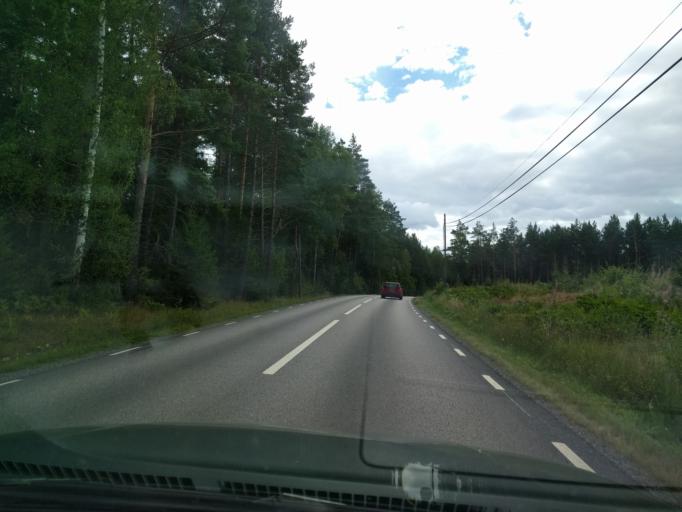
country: SE
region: Soedermanland
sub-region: Nykopings Kommun
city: Svalsta
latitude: 58.5248
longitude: 16.7674
